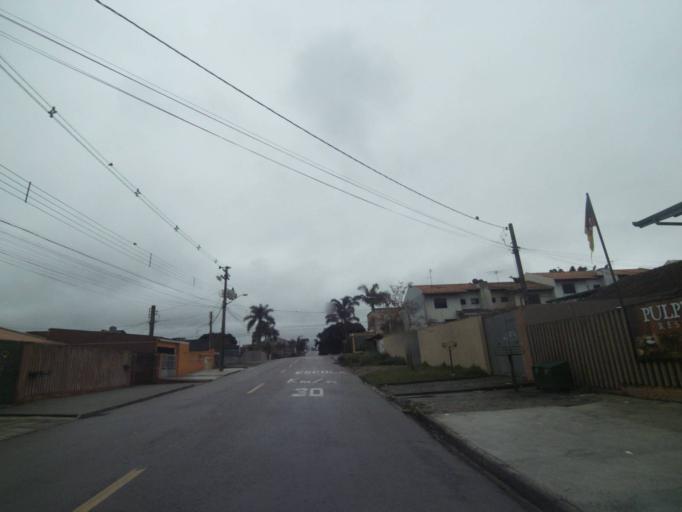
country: BR
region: Parana
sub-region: Curitiba
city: Curitiba
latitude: -25.5150
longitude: -49.3008
